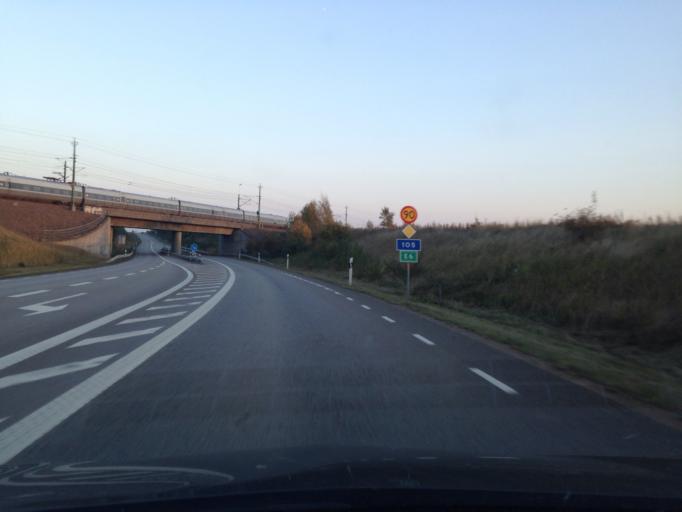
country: SE
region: Skane
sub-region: Bastads Kommun
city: Forslov
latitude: 56.3357
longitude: 12.8049
